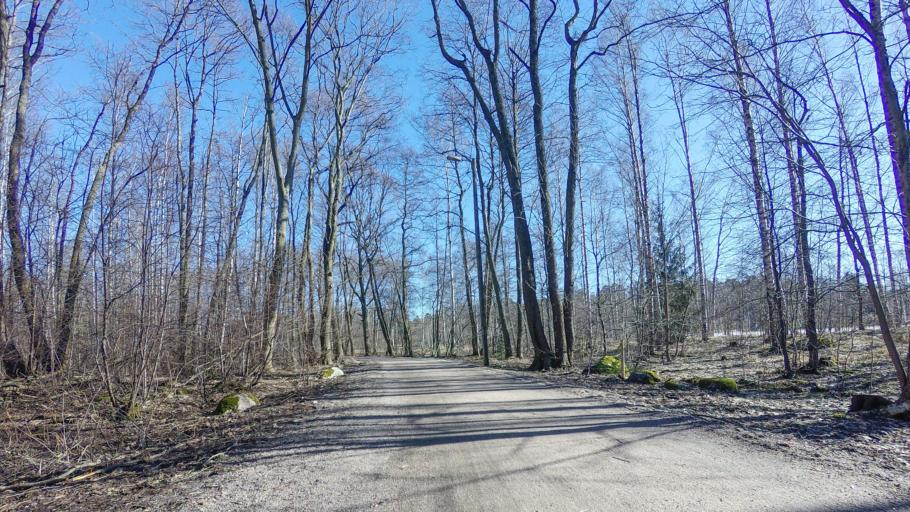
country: FI
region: Uusimaa
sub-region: Helsinki
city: Vantaa
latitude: 60.1939
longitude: 25.0601
